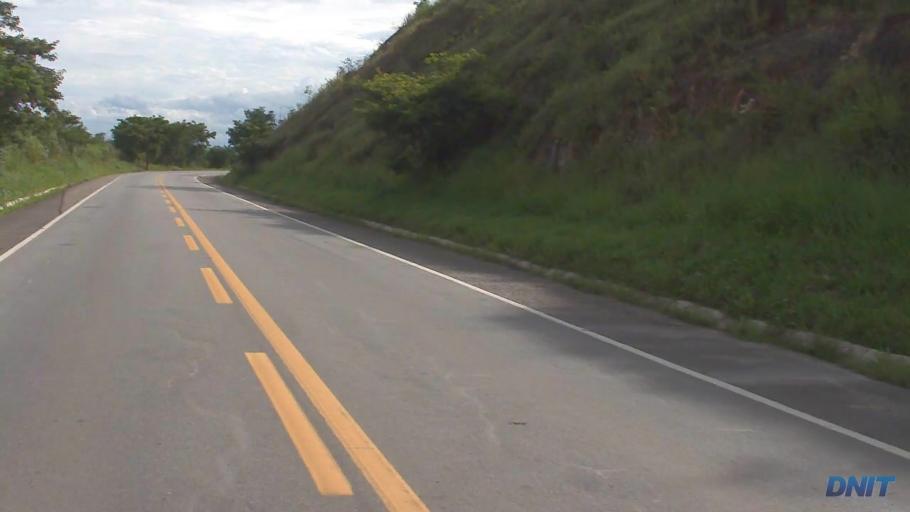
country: BR
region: Minas Gerais
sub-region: Belo Oriente
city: Belo Oriente
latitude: -19.1799
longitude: -42.2594
